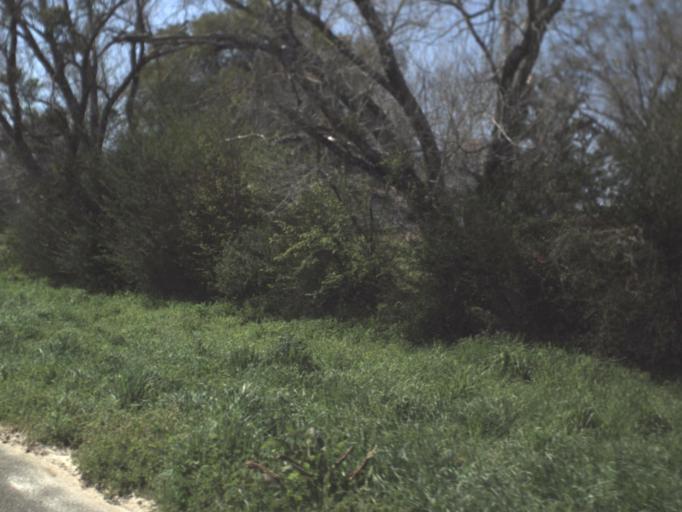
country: US
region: Florida
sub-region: Calhoun County
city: Blountstown
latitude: 30.5056
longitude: -85.0373
